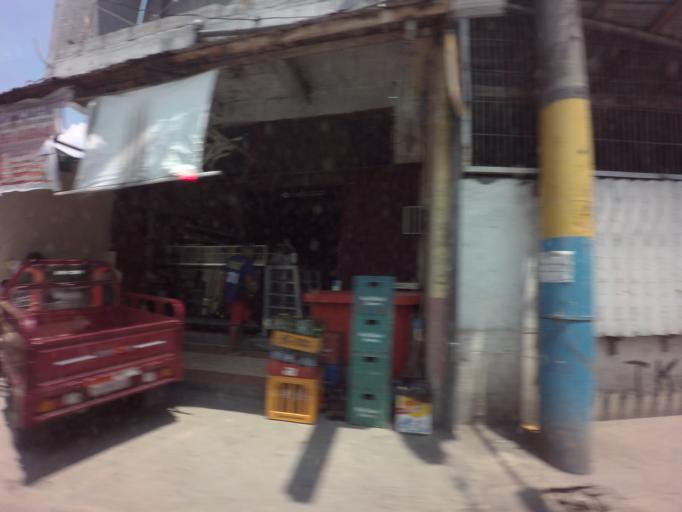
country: PH
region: Calabarzon
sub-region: Province of Laguna
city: San Pedro
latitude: 14.4049
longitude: 121.0502
